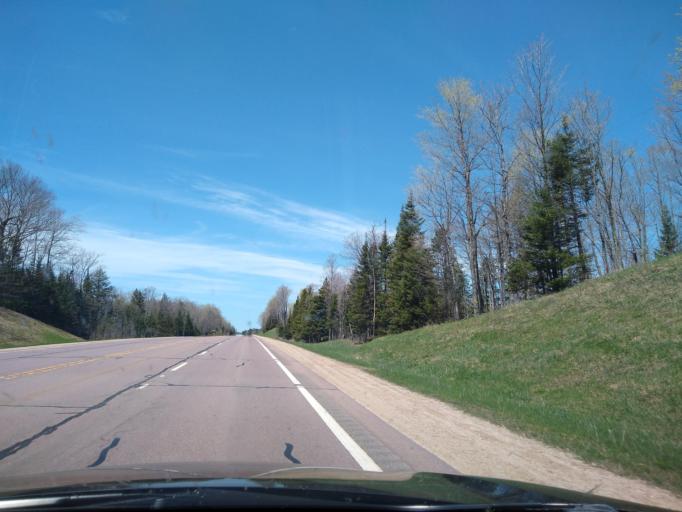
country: US
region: Michigan
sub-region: Marquette County
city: K. I. Sawyer Air Force Base
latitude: 46.2605
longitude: -87.0957
